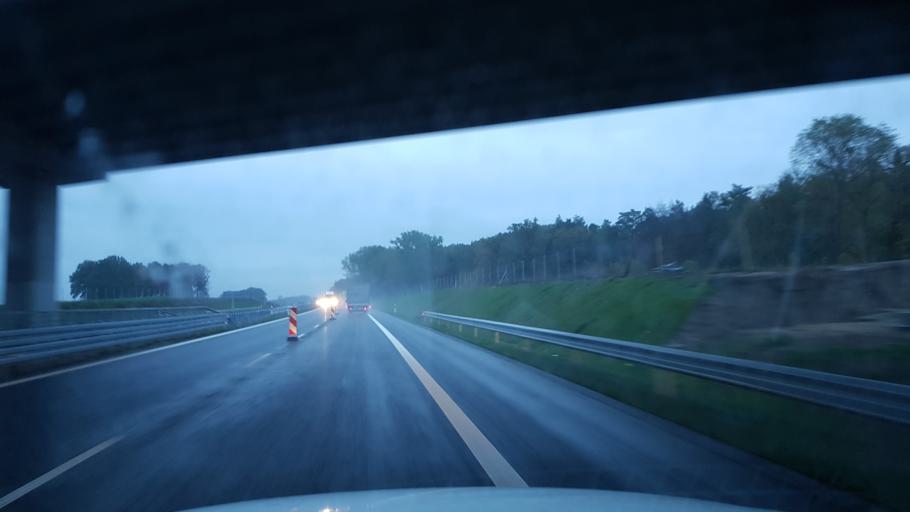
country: PL
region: West Pomeranian Voivodeship
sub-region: Powiat gryficki
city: Ploty
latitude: 53.8344
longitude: 15.2978
